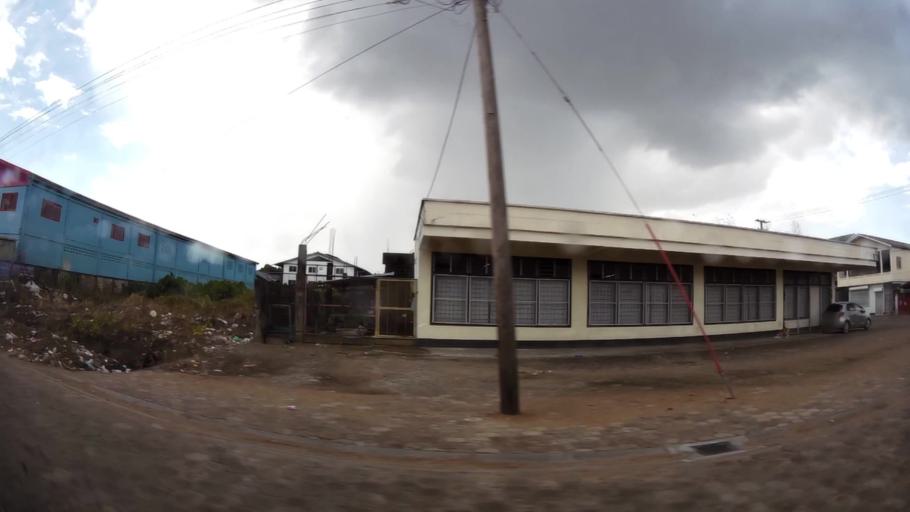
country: SR
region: Paramaribo
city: Paramaribo
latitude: 5.8340
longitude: -55.1452
